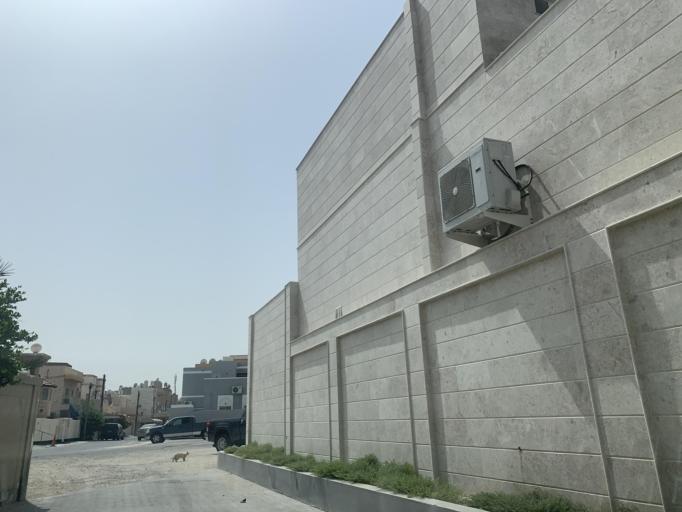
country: BH
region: Northern
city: Madinat `Isa
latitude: 26.1768
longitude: 50.5603
